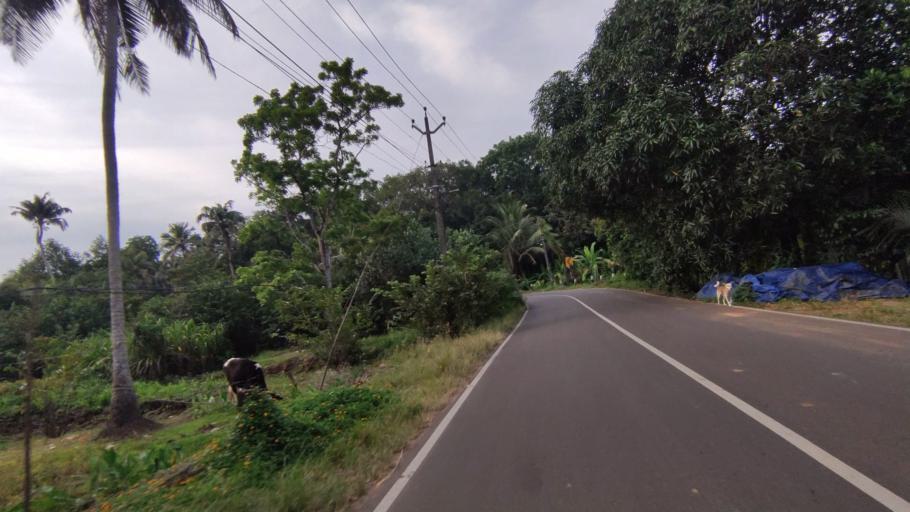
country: IN
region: Kerala
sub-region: Kottayam
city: Kottayam
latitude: 9.6382
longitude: 76.4890
